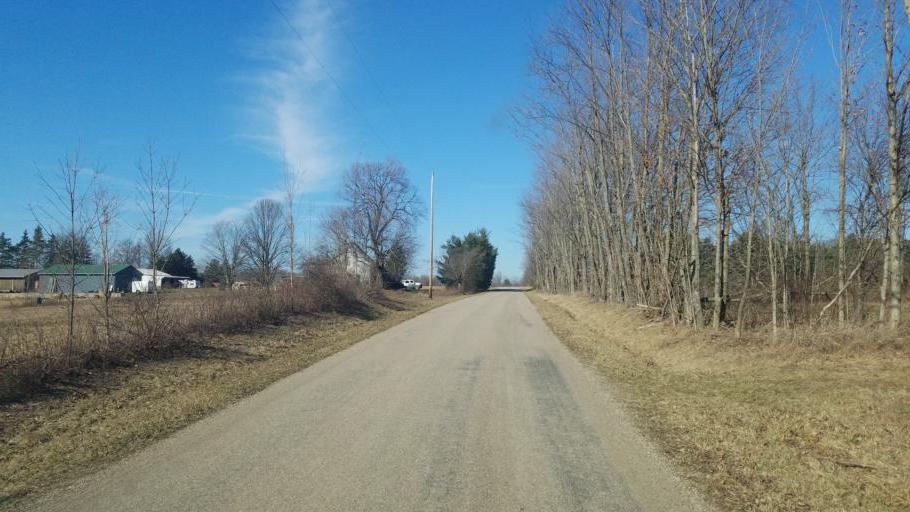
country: US
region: Ohio
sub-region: Sandusky County
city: Bellville
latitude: 40.5724
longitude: -82.5804
